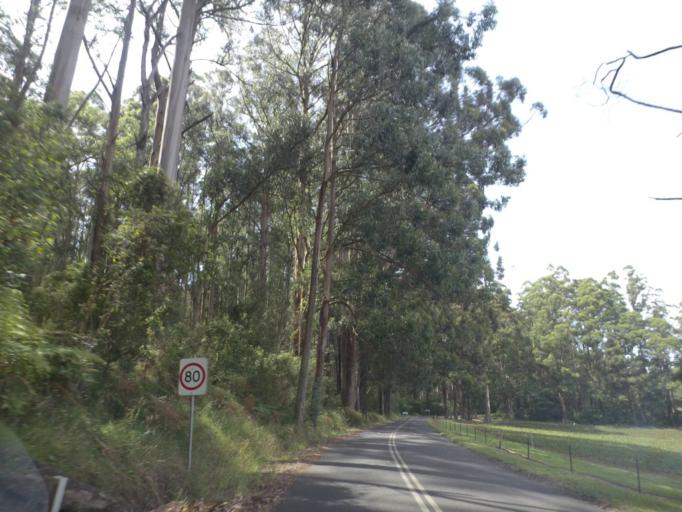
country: AU
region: Victoria
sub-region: Yarra Ranges
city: Healesville
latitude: -37.5622
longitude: 145.5079
